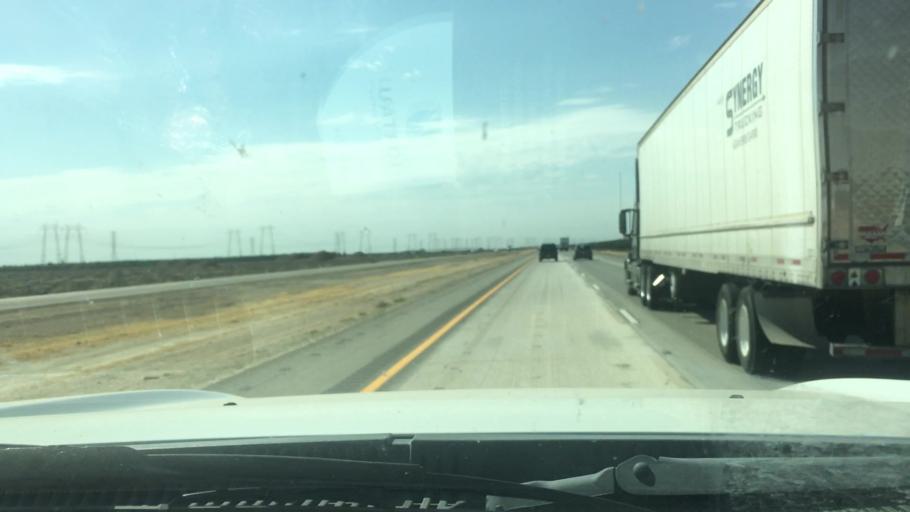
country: US
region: California
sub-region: Kern County
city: Buttonwillow
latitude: 35.5204
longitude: -119.5572
